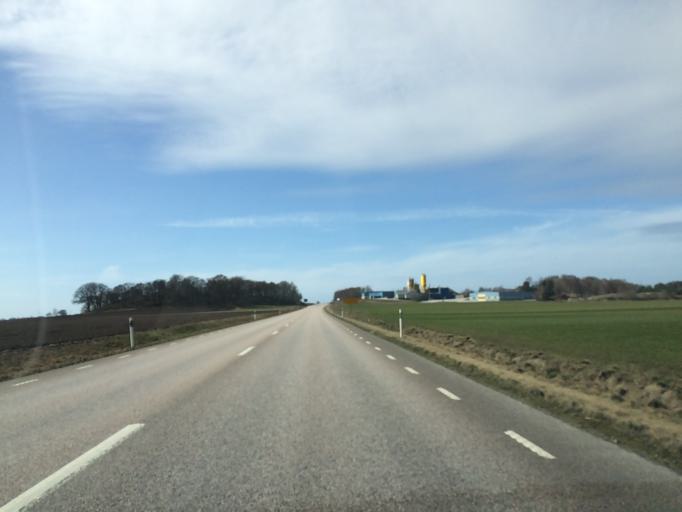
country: SE
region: Halland
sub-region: Laholms Kommun
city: Veinge
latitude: 56.5431
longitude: 13.0972
